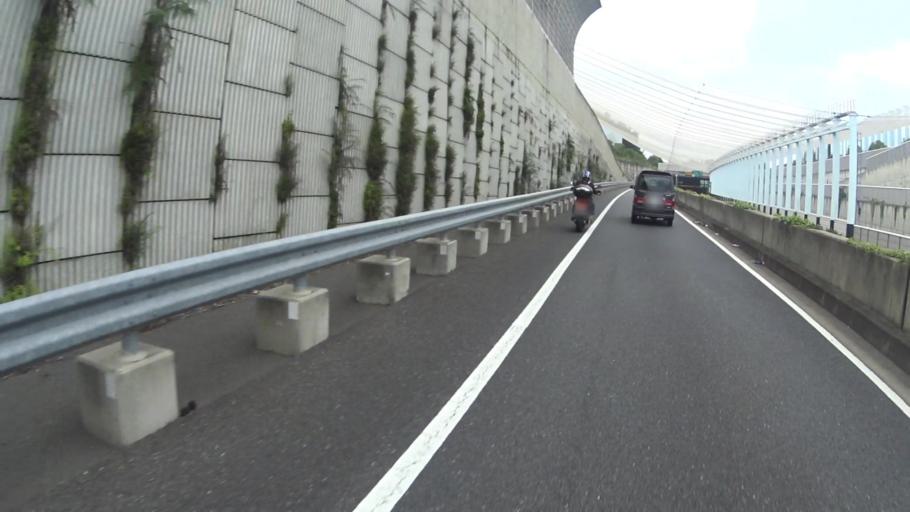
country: JP
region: Kyoto
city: Tanabe
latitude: 34.8269
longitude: 135.7239
